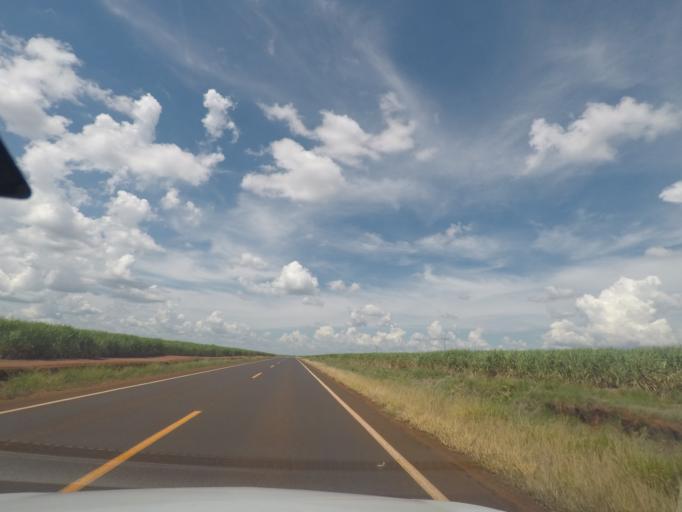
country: BR
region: Minas Gerais
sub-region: Conceicao Das Alagoas
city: Conceicao das Alagoas
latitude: -19.8640
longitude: -48.6072
